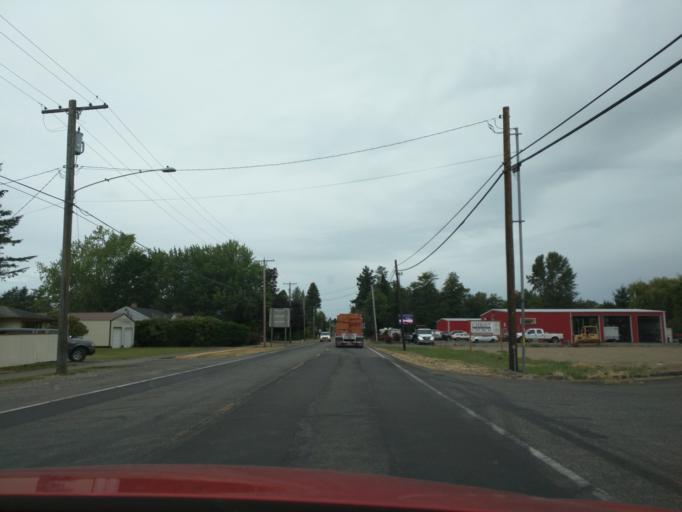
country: US
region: Washington
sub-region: Whatcom County
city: Nooksack
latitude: 48.9218
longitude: -122.3219
